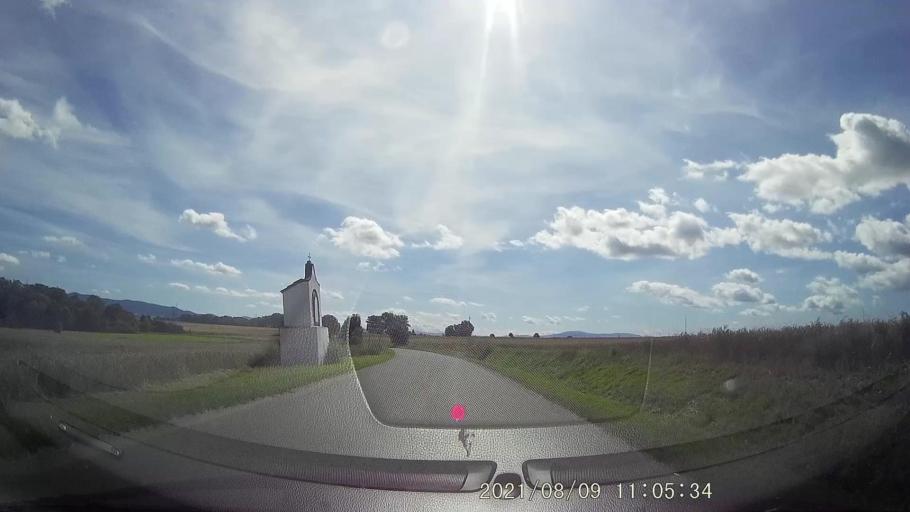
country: PL
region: Lower Silesian Voivodeship
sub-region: Powiat klodzki
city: Bozkow
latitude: 50.4599
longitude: 16.5797
